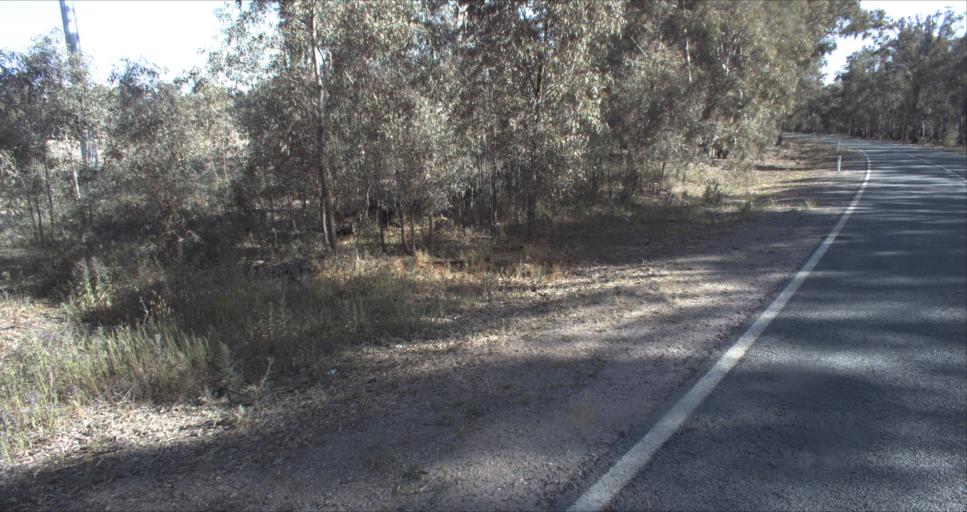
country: AU
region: New South Wales
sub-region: Leeton
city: Leeton
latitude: -34.6244
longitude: 146.3810
